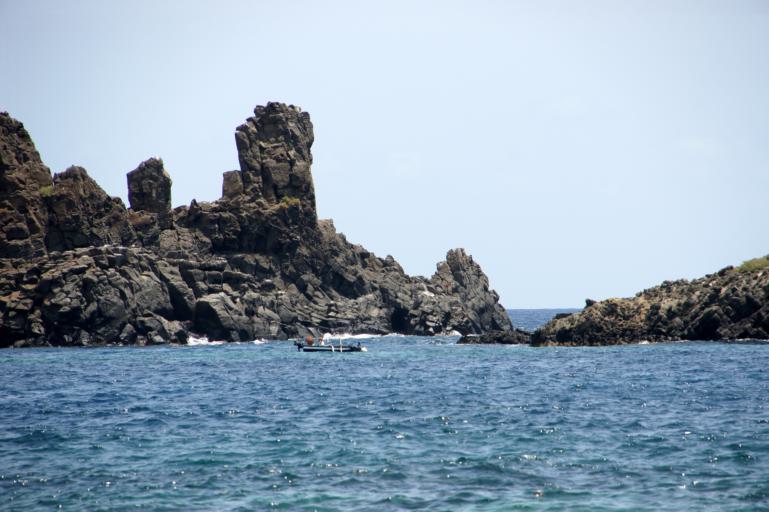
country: IT
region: Sicily
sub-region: Catania
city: Acitrezza
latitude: 37.5593
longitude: 15.1608
